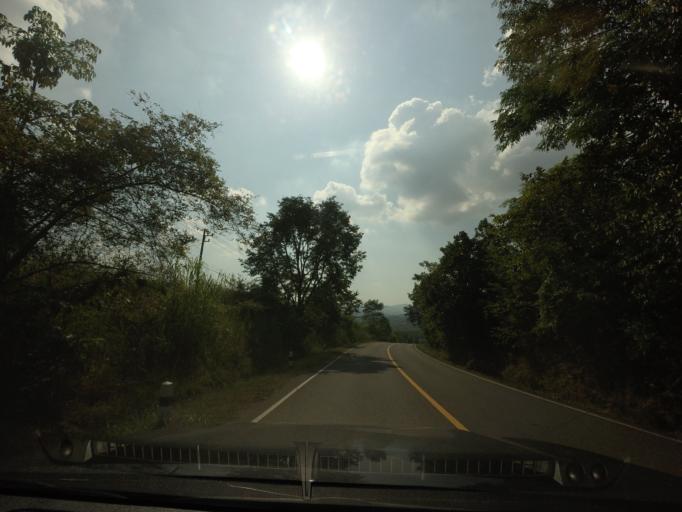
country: TH
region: Nan
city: Santi Suk
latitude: 18.9825
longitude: 100.9453
